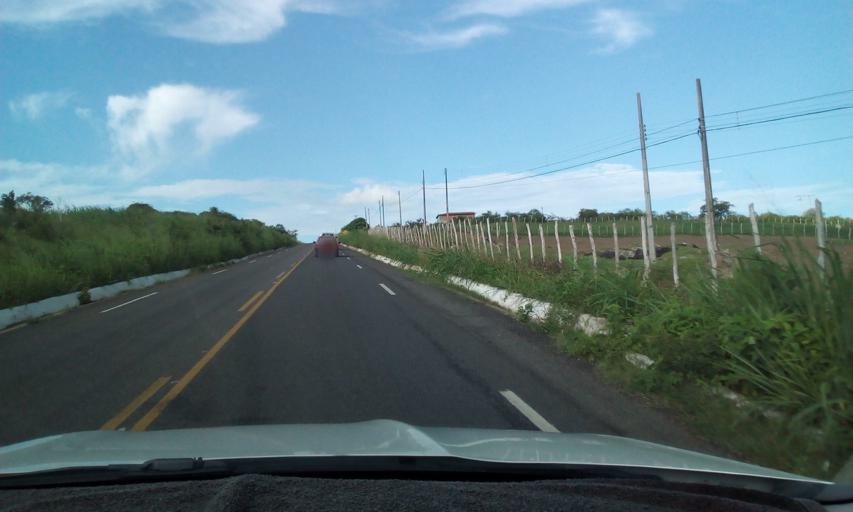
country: BR
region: Paraiba
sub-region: Guarabira
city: Guarabira
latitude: -6.8477
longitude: -35.3632
